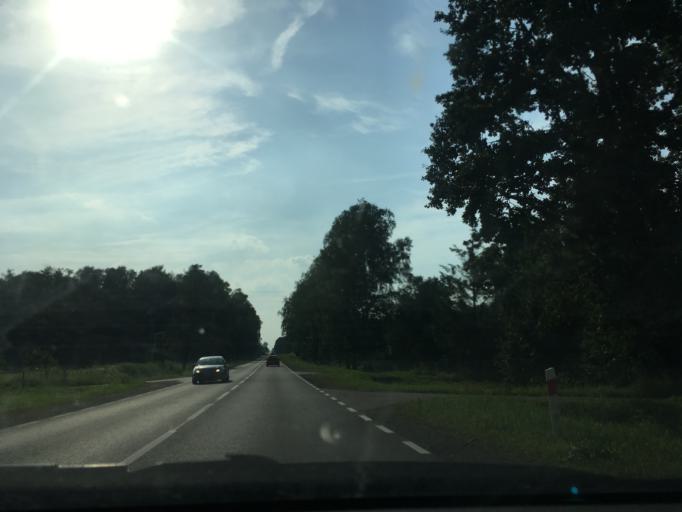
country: PL
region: Podlasie
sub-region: Powiat bialostocki
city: Suprasl
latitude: 53.1255
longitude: 23.3068
